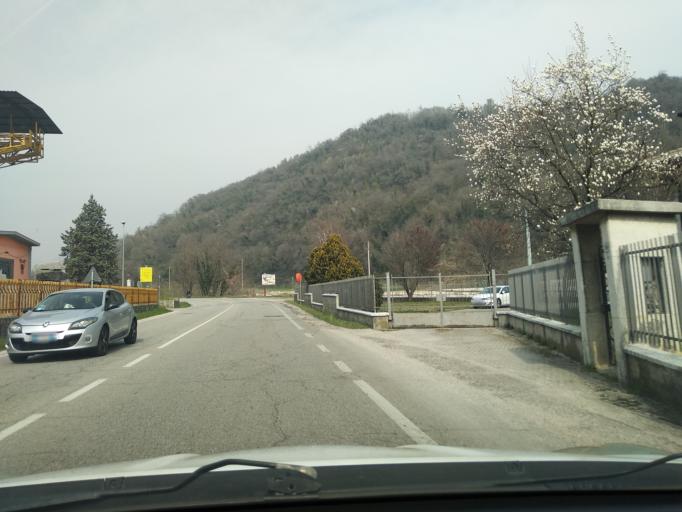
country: IT
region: Veneto
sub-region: Provincia di Vicenza
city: Chiampo
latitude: 45.5568
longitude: 11.2712
